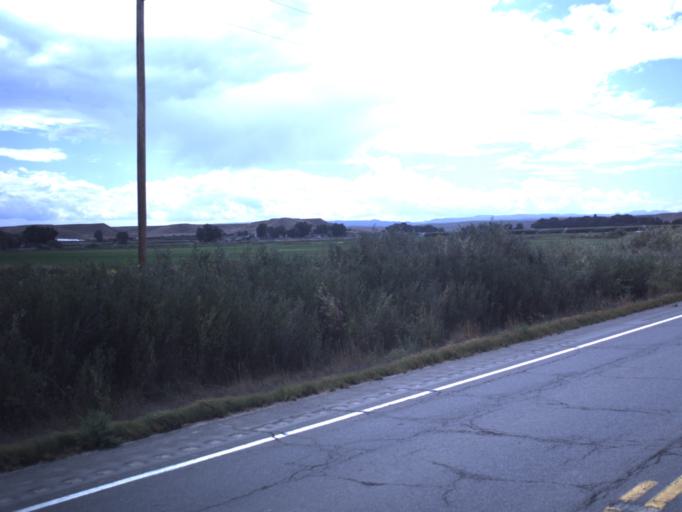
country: US
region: Utah
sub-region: Duchesne County
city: Duchesne
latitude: 40.1569
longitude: -110.1874
